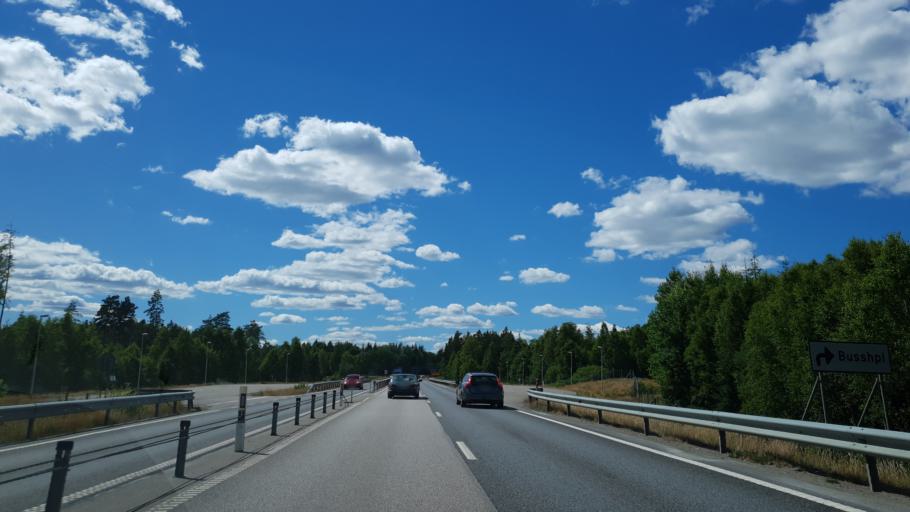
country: SE
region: Kronoberg
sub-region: Vaxjo Kommun
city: Ingelstad
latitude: 56.8713
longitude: 14.9540
